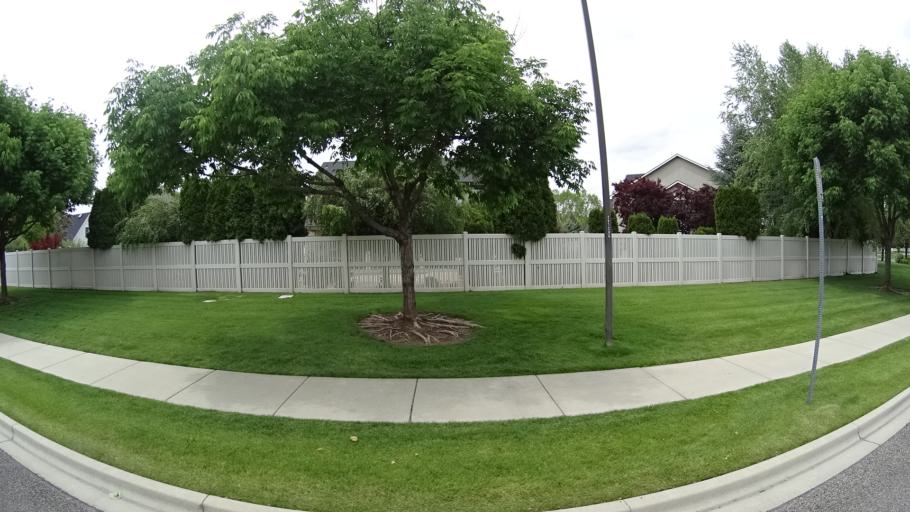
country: US
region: Idaho
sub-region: Ada County
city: Meridian
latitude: 43.6424
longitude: -116.4238
